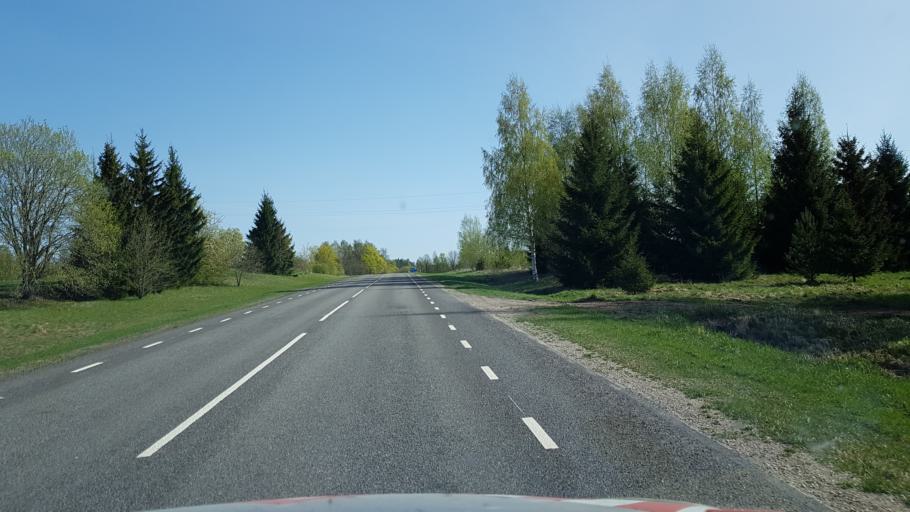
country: EE
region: Viljandimaa
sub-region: Viljandi linn
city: Viljandi
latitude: 58.2372
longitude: 25.5876
